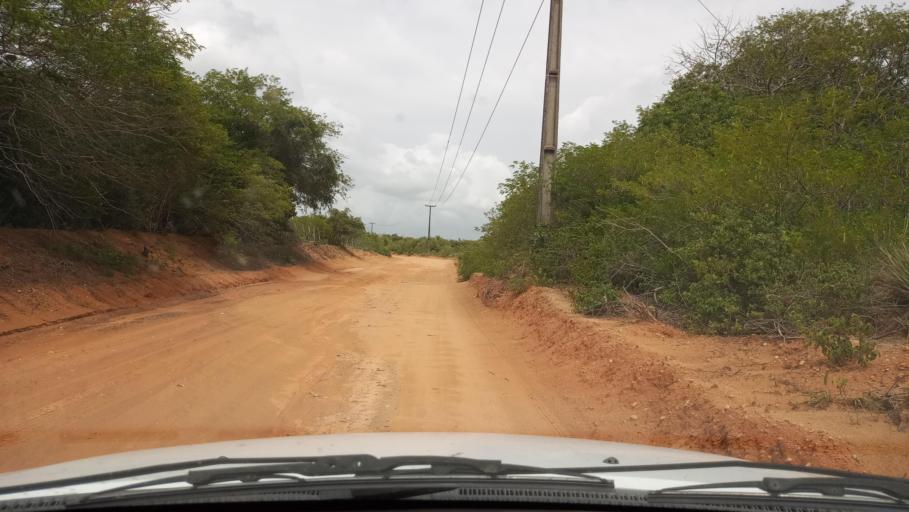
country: BR
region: Rio Grande do Norte
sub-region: Maxaranguape
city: Sao Miguel
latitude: -5.4830
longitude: -35.3185
